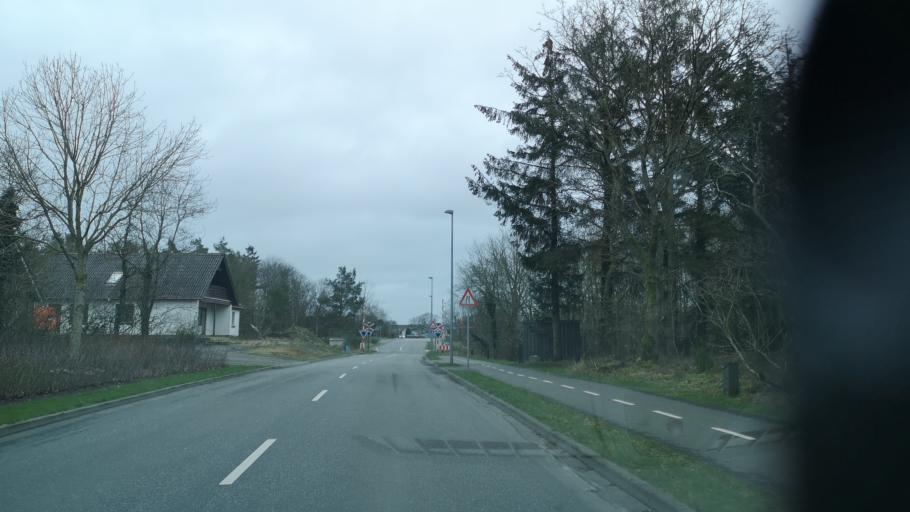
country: DK
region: Central Jutland
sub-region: Ringkobing-Skjern Kommune
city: Skjern
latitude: 55.9350
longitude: 8.5027
